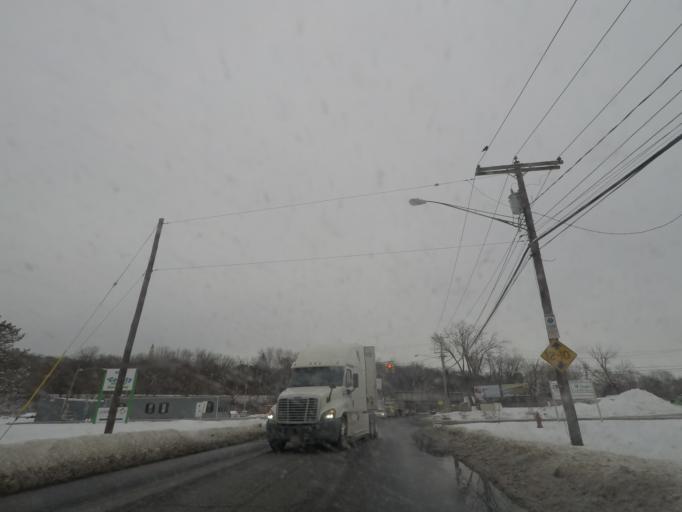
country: US
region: New York
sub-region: Albany County
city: Albany
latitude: 42.6245
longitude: -73.7685
